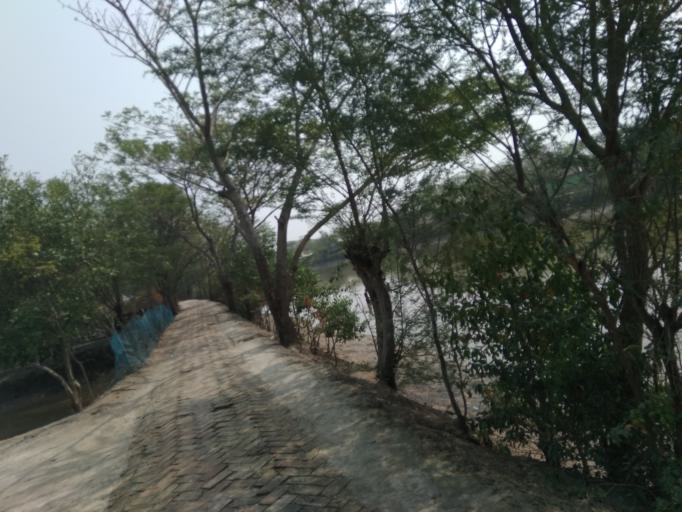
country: IN
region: West Bengal
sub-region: North 24 Parganas
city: Gosaba
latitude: 22.2562
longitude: 89.2531
